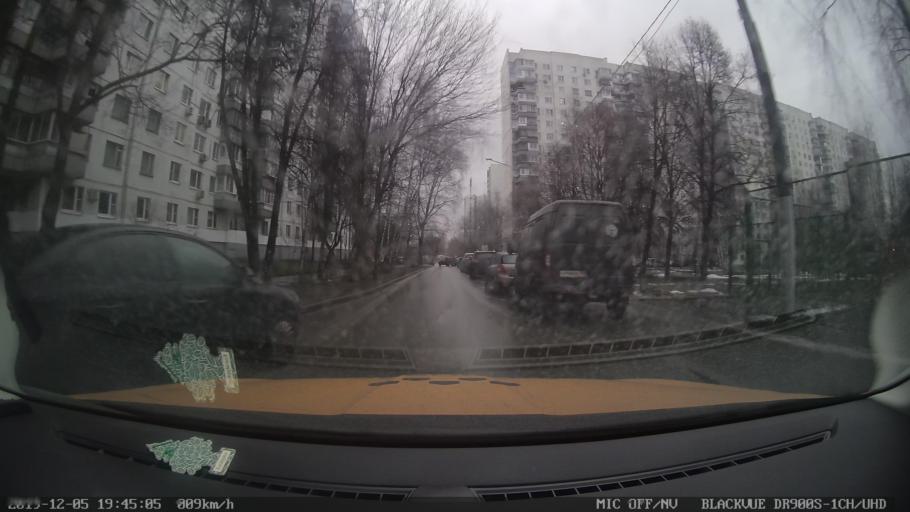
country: RU
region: Moscow
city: Lianozovo
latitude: 55.9018
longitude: 37.5770
